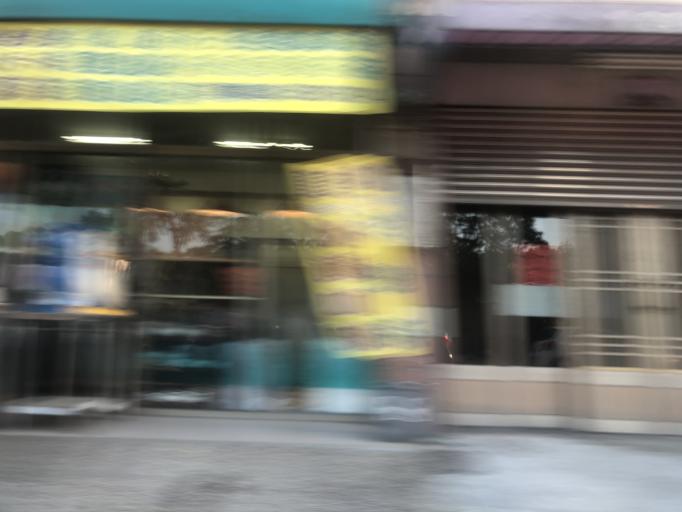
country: TW
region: Taiwan
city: Fengyuan
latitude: 24.2767
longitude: 120.7759
